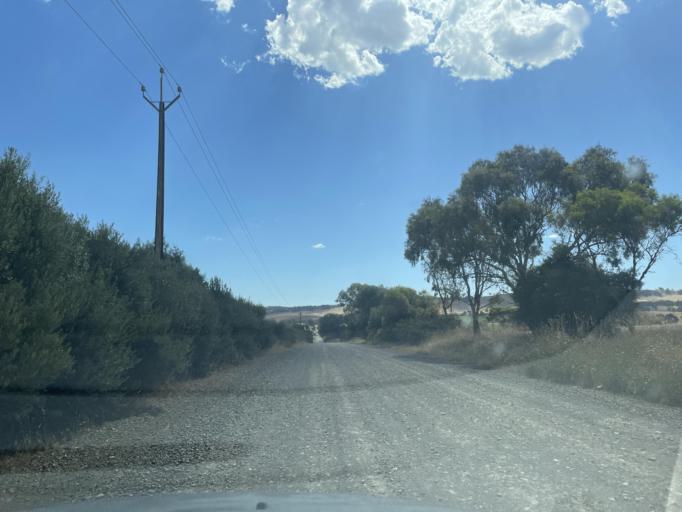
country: AU
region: South Australia
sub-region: Clare and Gilbert Valleys
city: Clare
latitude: -33.9100
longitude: 138.7305
